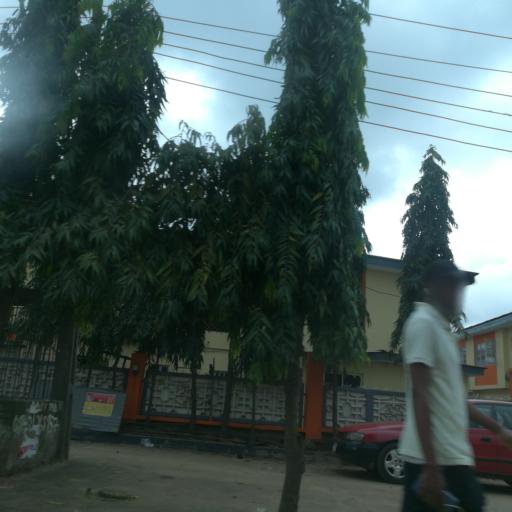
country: NG
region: Lagos
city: Agege
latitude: 6.6132
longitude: 3.2989
